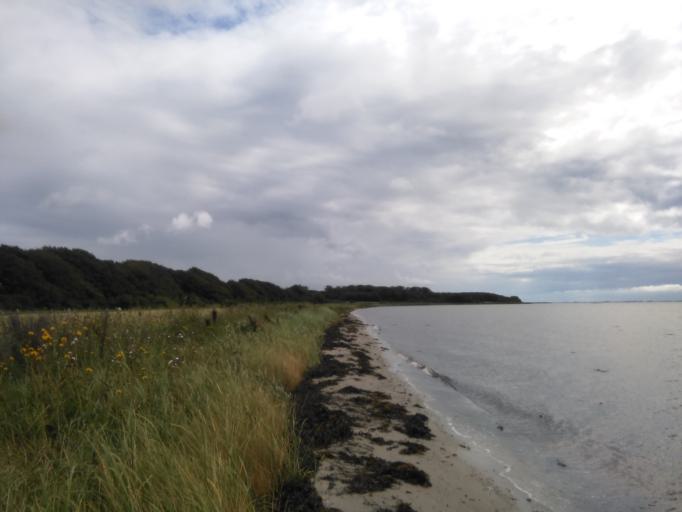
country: DK
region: Central Jutland
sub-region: Odder Kommune
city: Odder
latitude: 55.8571
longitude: 10.1429
